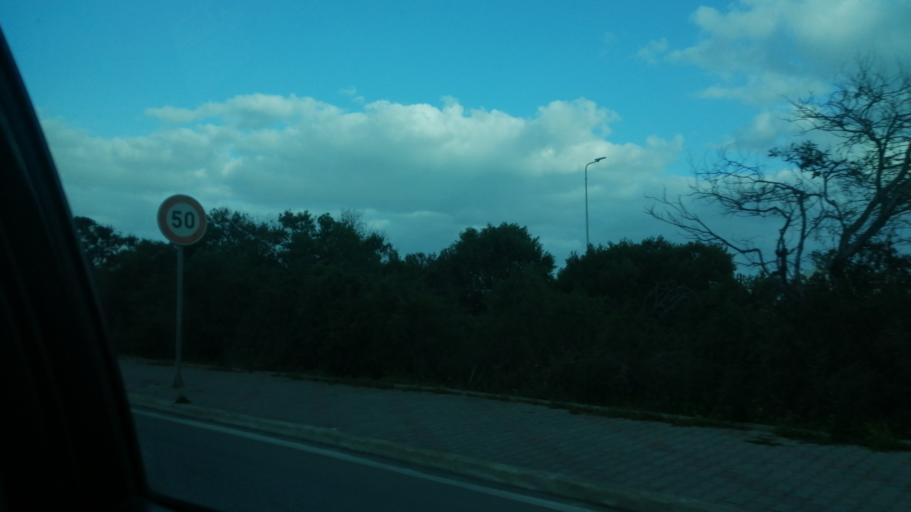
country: TN
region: Tunis
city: Al Marsa
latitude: 36.9192
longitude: 10.2937
